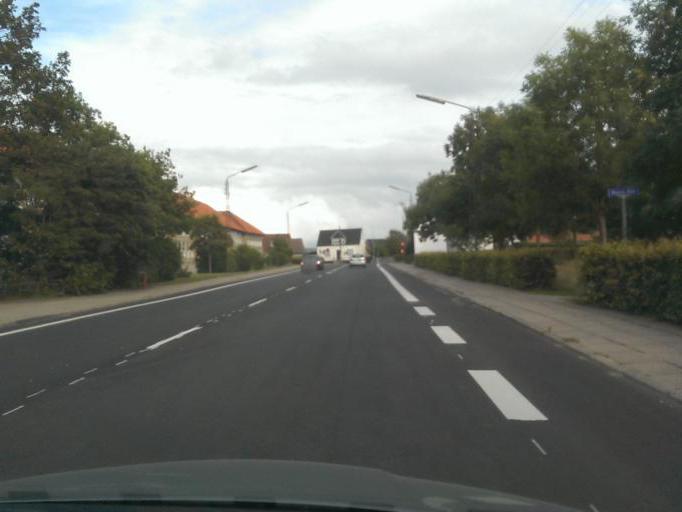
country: DK
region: North Denmark
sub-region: Hjorring Kommune
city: Hjorring
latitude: 57.4657
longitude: 9.9815
